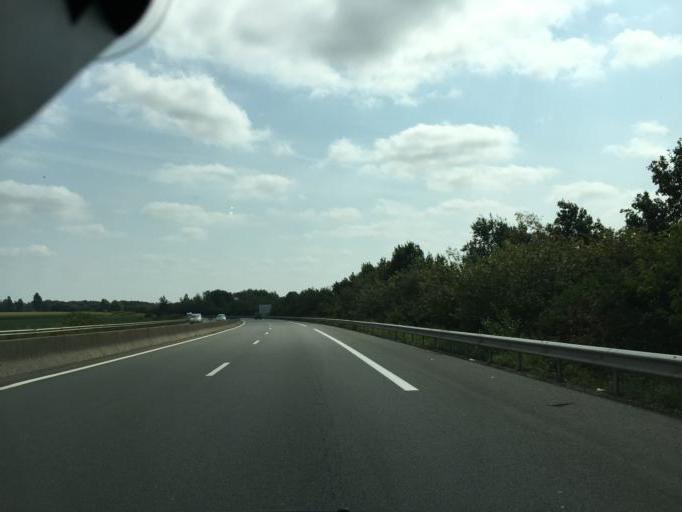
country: FR
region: Nord-Pas-de-Calais
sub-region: Departement du Nord
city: Somain
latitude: 50.3524
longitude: 3.2630
